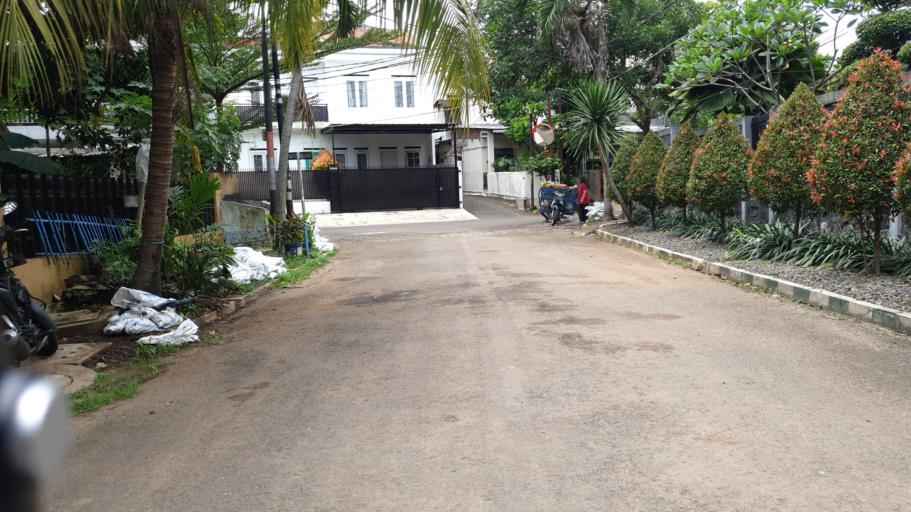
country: ID
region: West Java
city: Pamulang
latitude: -6.2975
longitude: 106.7777
